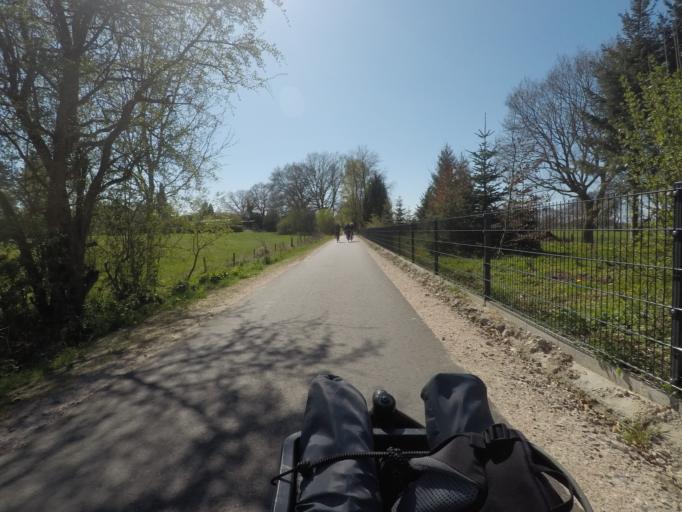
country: DE
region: Schleswig-Holstein
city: Siek
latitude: 53.6094
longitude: 10.2883
